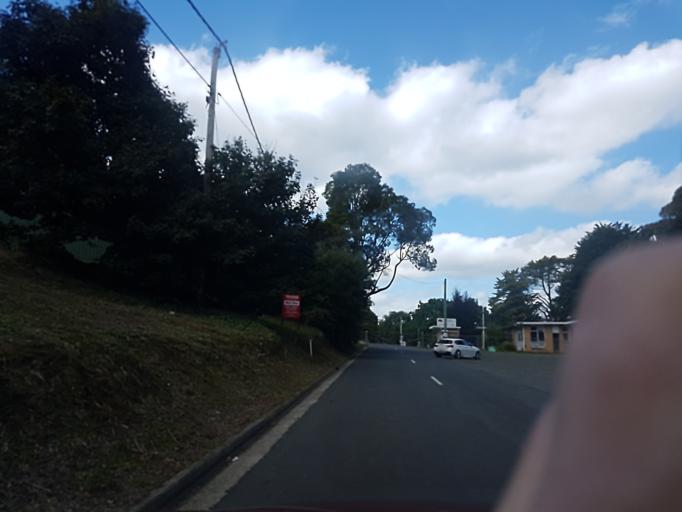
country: AU
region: Victoria
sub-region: Yarra Ranges
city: Monbulk
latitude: -37.8828
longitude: 145.4014
